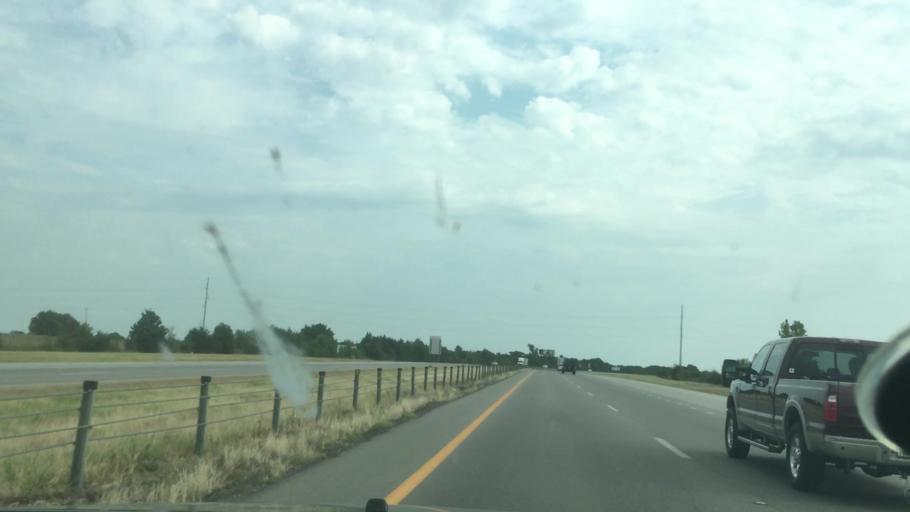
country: US
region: Oklahoma
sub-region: Bryan County
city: Calera
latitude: 33.9734
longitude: -96.4168
